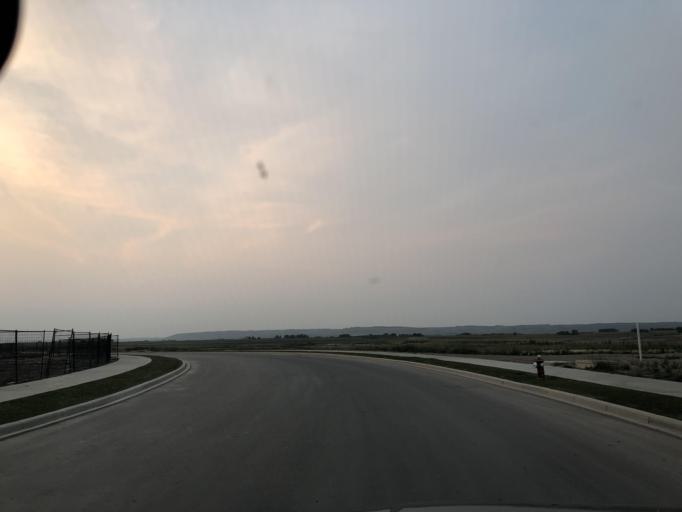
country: CA
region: Alberta
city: Cochrane
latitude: 51.1146
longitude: -114.3983
